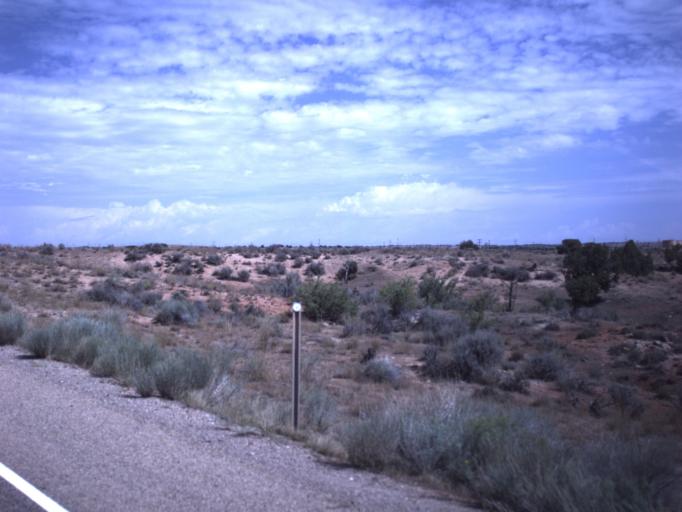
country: US
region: Utah
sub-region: Uintah County
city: Naples
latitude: 40.1680
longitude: -109.3164
